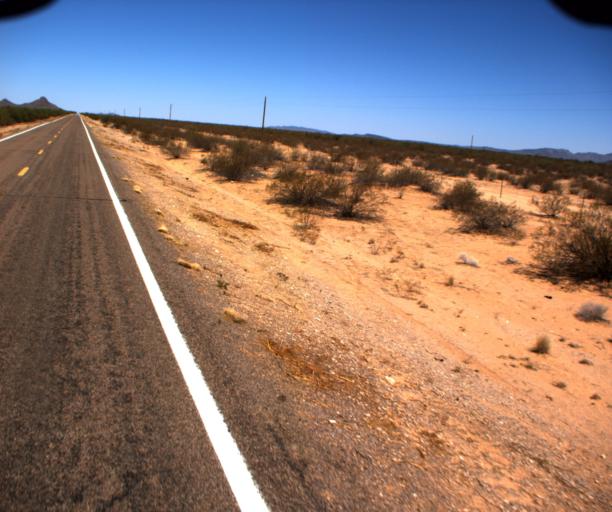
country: US
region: Arizona
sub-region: Pima County
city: Ajo
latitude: 32.1967
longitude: -112.4656
